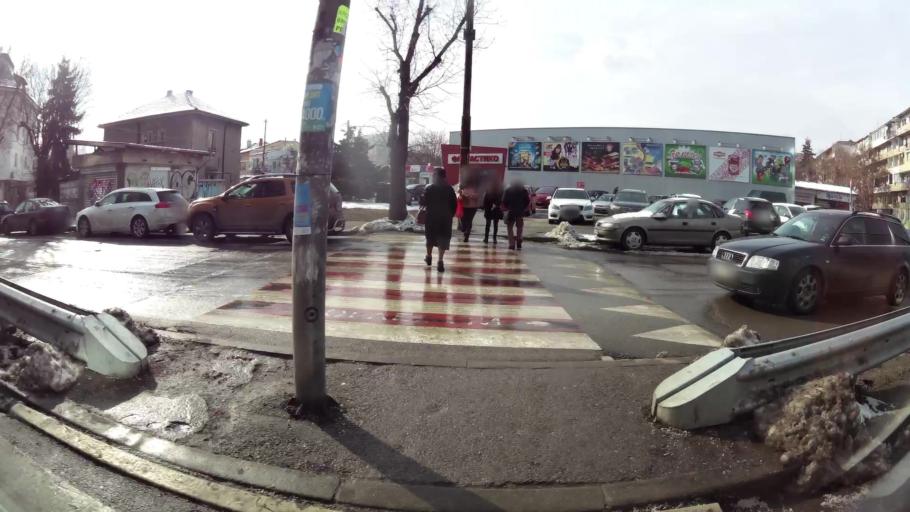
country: BG
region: Sofia-Capital
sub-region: Stolichna Obshtina
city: Sofia
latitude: 42.7092
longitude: 23.3562
